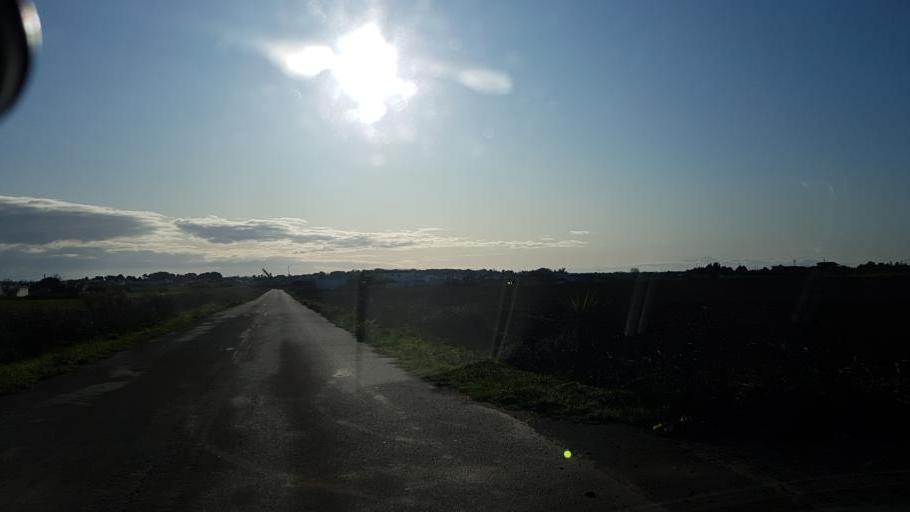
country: IT
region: Apulia
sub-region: Provincia di Brindisi
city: Torchiarolo
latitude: 40.5355
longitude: 18.0667
